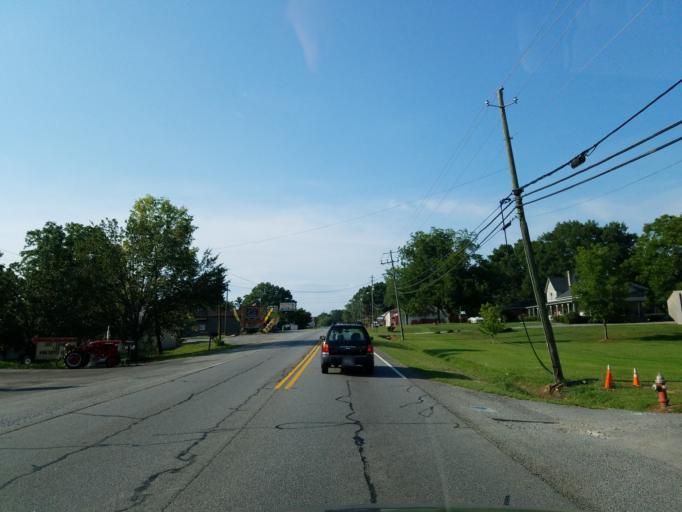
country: US
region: Georgia
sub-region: Bartow County
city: Rydal
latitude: 34.2802
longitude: -84.7436
